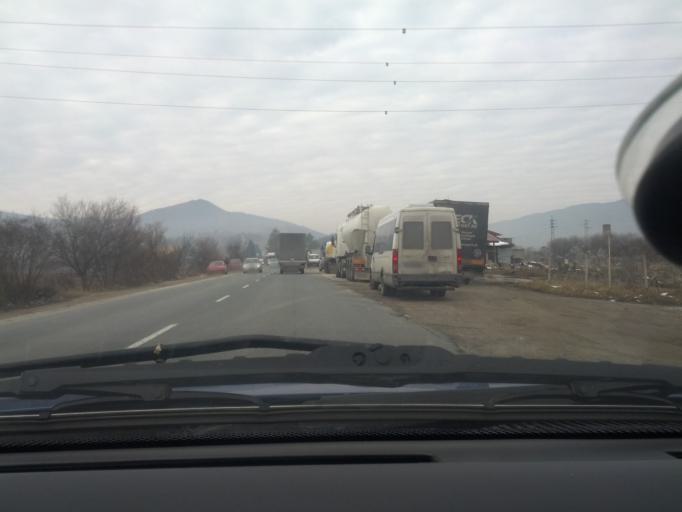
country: BG
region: Sofiya
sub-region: Obshtina Botevgrad
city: Botevgrad
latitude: 42.9756
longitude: 23.7429
